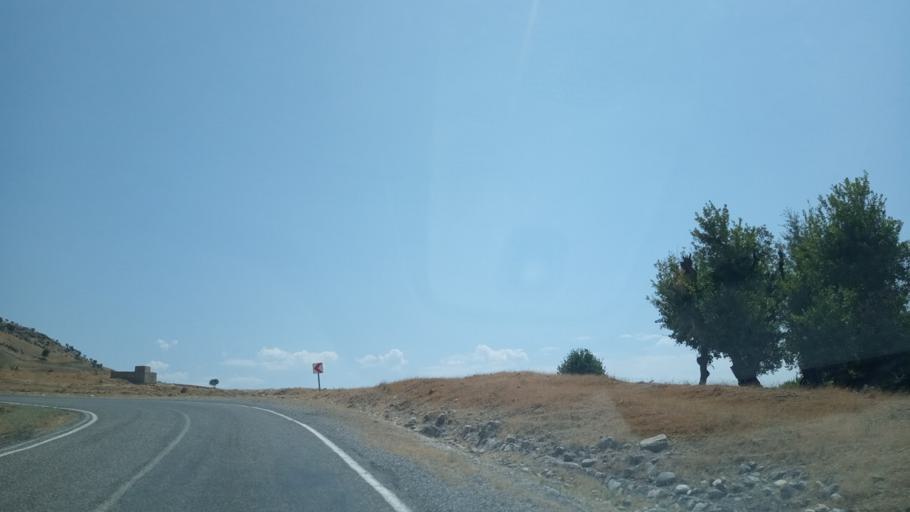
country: TR
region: Siirt
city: Dilektepe
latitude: 38.0631
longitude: 41.8324
